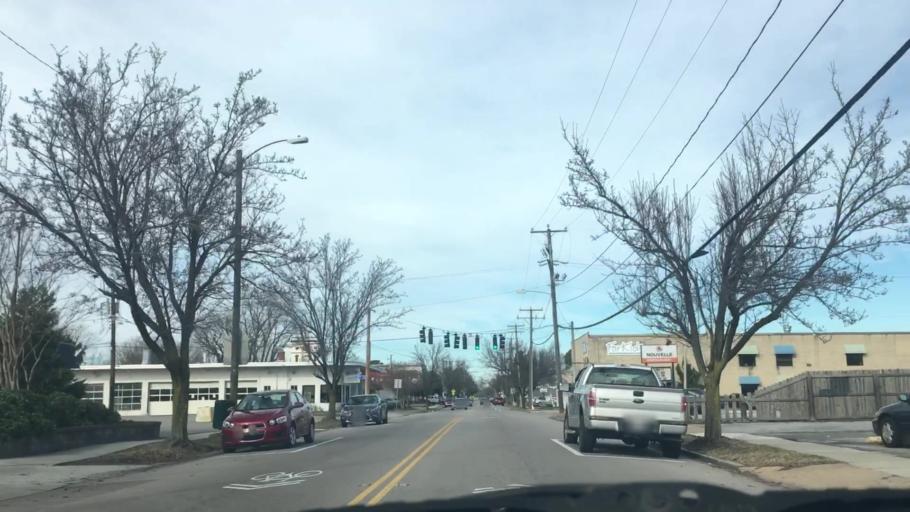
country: US
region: Virginia
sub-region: City of Norfolk
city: Norfolk
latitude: 36.8823
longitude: -76.2948
